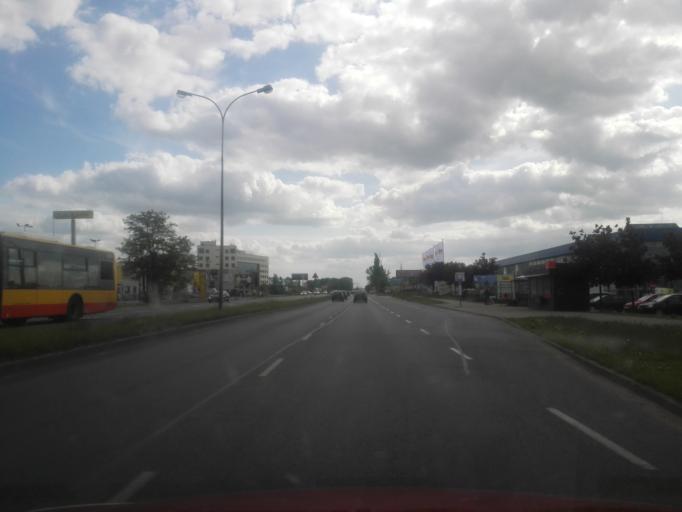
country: PL
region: Masovian Voivodeship
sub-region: Powiat wolominski
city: Zabki
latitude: 52.3031
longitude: 21.0886
